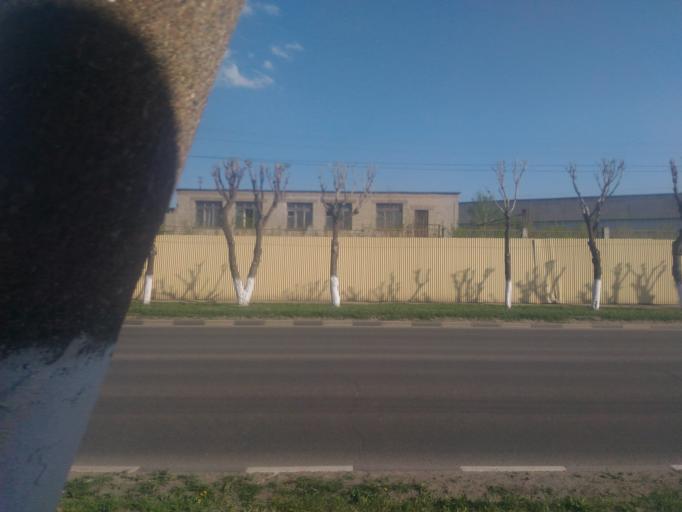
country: RU
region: Ulyanovsk
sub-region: Ulyanovskiy Rayon
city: Ulyanovsk
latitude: 54.2801
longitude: 48.3455
